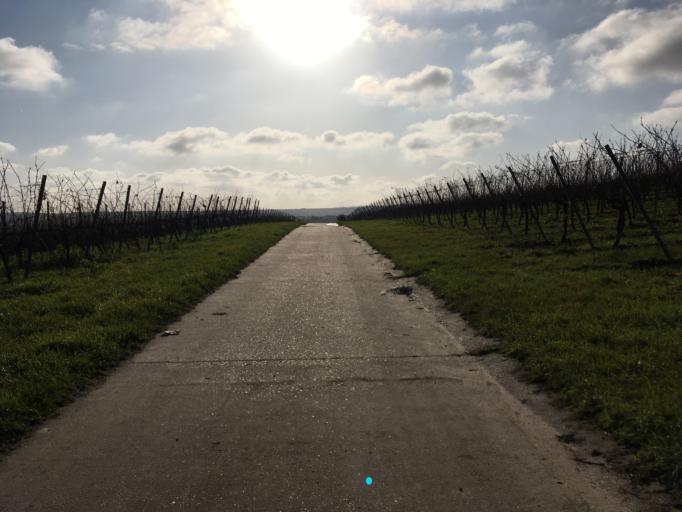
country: DE
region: Rheinland-Pfalz
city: Bodenheim
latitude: 49.9419
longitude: 8.3023
